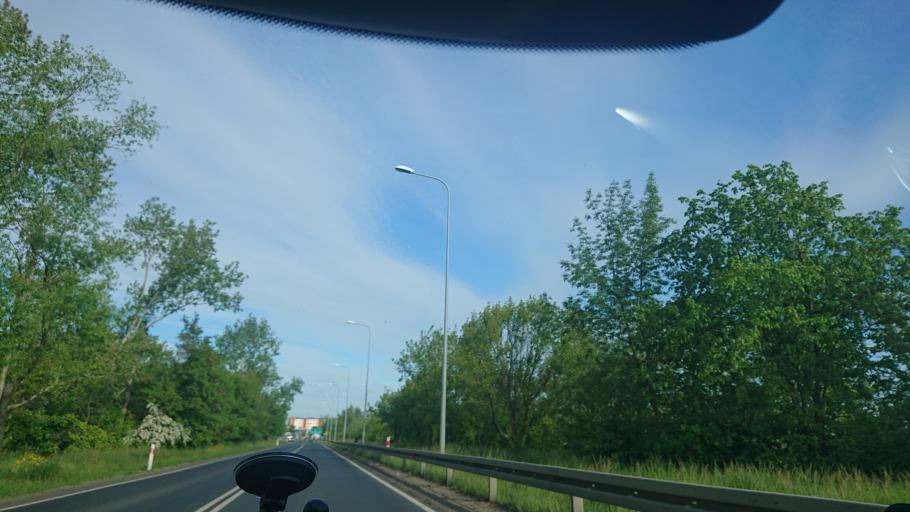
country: PL
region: Greater Poland Voivodeship
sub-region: Powiat gnieznienski
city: Gniezno
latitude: 52.5152
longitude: 17.5884
